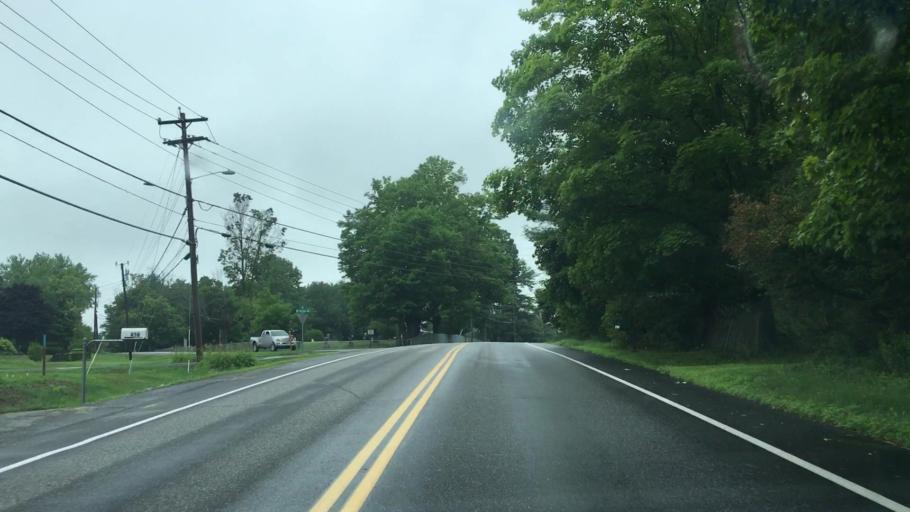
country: US
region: Maine
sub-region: Kennebec County
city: Augusta
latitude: 44.3421
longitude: -69.8087
